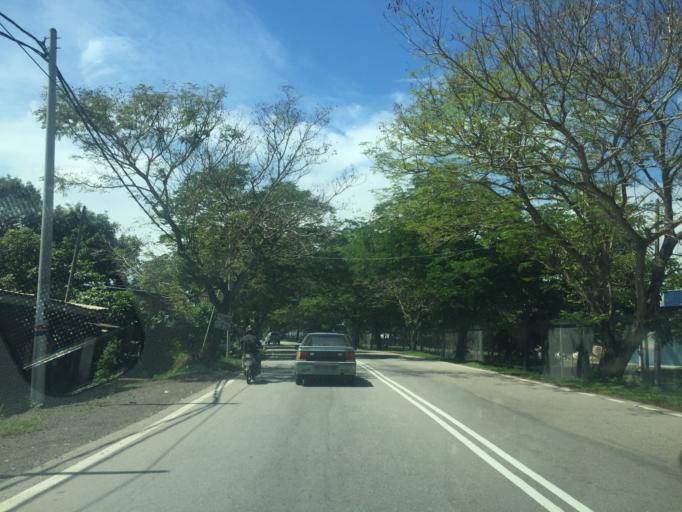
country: MY
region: Penang
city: Permatang Kuching
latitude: 5.4524
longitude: 100.4355
